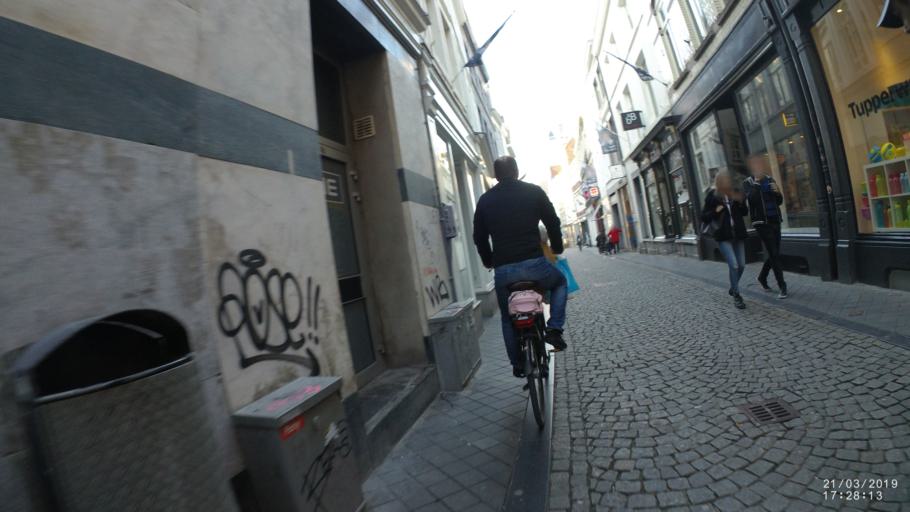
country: NL
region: Limburg
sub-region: Gemeente Maastricht
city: Maastricht
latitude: 50.8500
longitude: 5.6914
